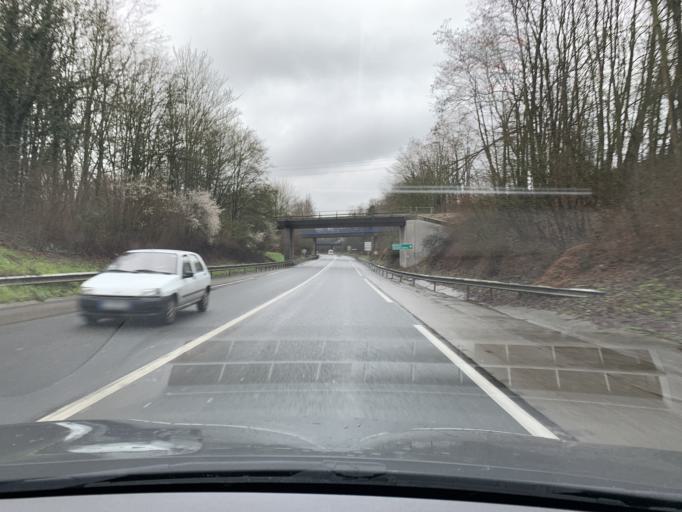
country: FR
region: Nord-Pas-de-Calais
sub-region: Departement du Nord
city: Dechy
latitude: 50.3498
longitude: 3.1191
